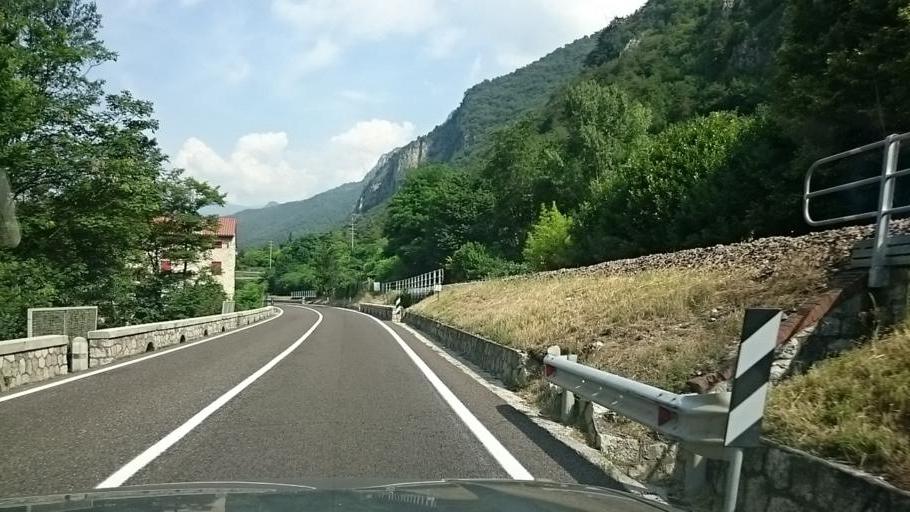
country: IT
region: Veneto
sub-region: Provincia di Vicenza
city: Campolongo sul Brenta
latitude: 45.8301
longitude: 11.7028
